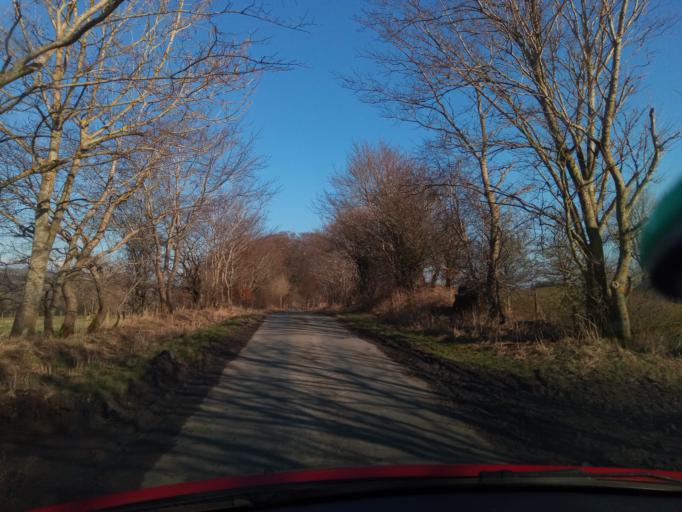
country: GB
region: Scotland
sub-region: The Scottish Borders
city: Hawick
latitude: 55.5025
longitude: -2.7681
